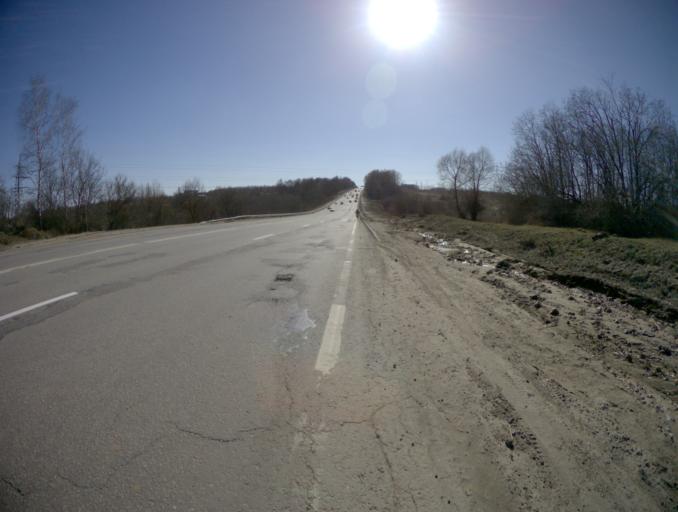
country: RU
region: Vladimir
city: Bogolyubovo
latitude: 56.1825
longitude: 40.5103
